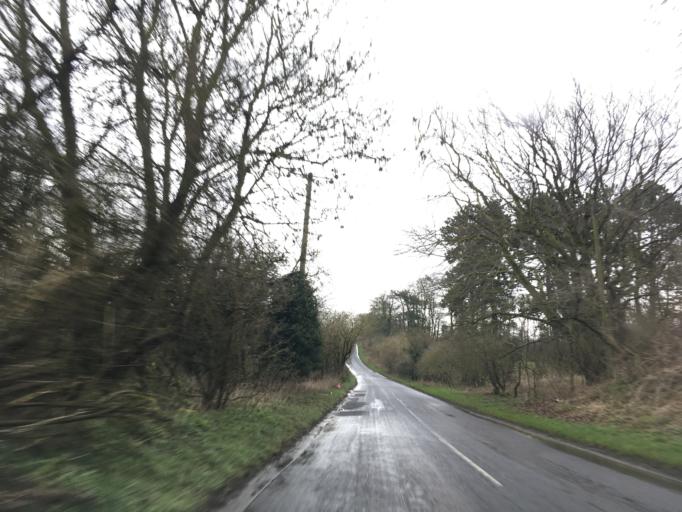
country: GB
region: England
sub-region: Borough of Swindon
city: Wanborough
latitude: 51.5375
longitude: -1.6779
